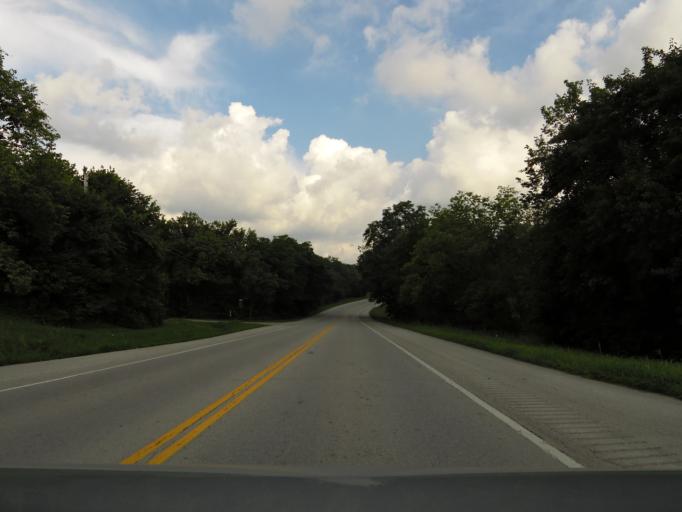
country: US
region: Kentucky
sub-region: Bourbon County
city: Paris
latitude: 38.2345
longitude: -84.2778
